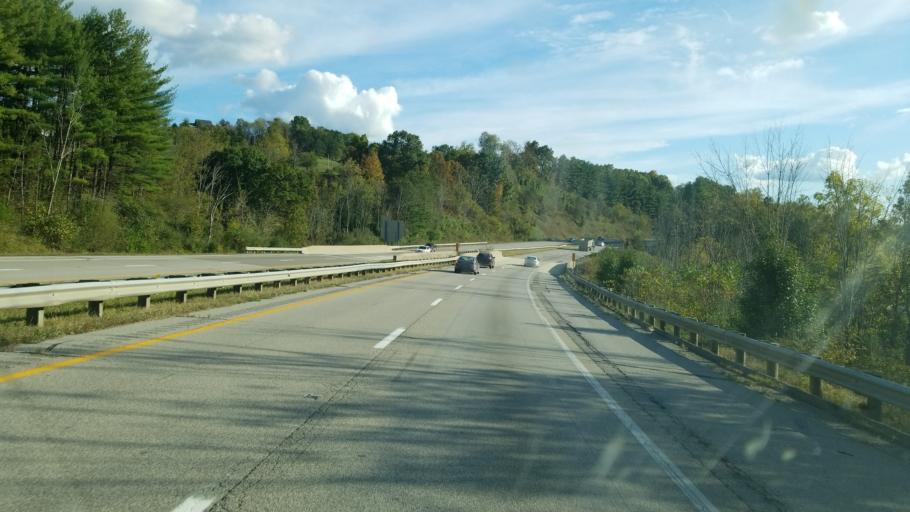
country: US
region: Ohio
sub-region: Washington County
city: Devola
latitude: 39.4695
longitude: -81.4360
